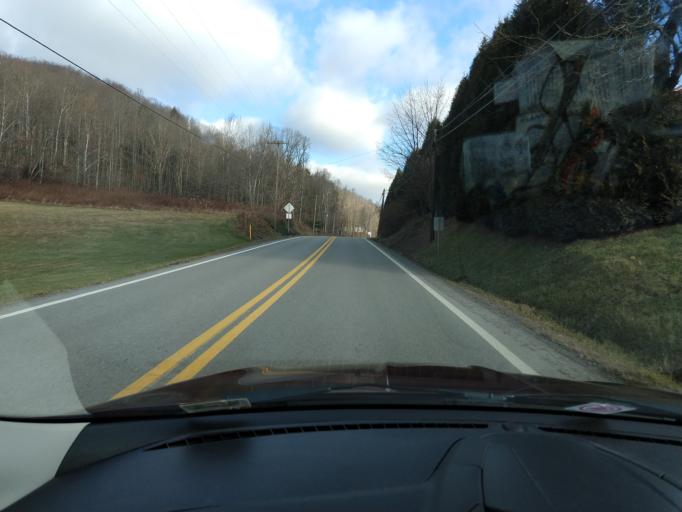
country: US
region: West Virginia
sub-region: Randolph County
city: Elkins
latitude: 38.7503
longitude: -79.9585
